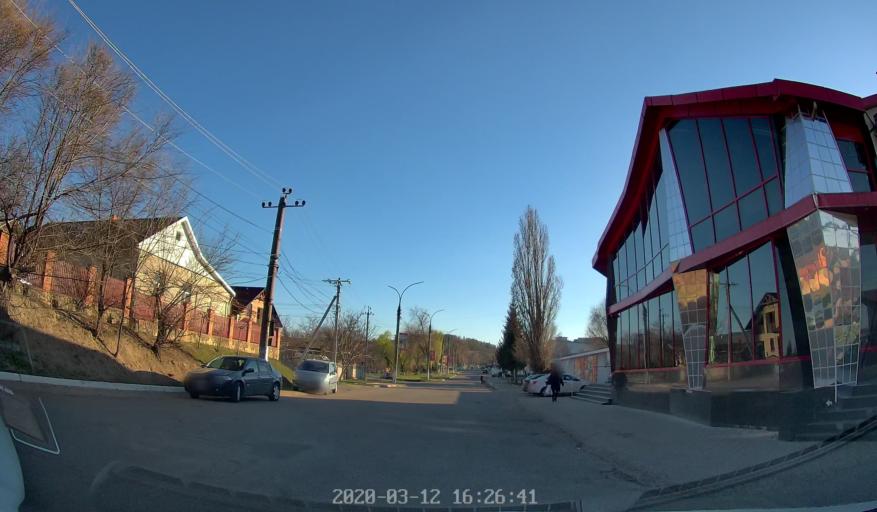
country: MD
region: Anenii Noi
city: Anenii Noi
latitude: 46.8802
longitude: 29.2323
